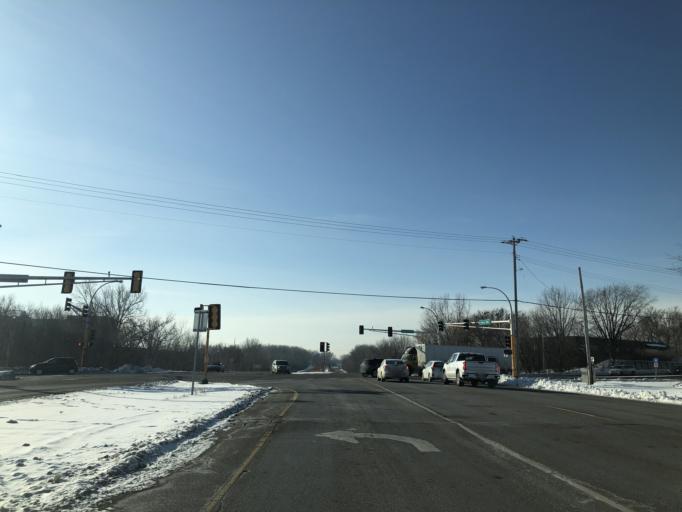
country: US
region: Minnesota
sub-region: Hennepin County
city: Saint Anthony
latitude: 45.0362
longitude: -93.1967
